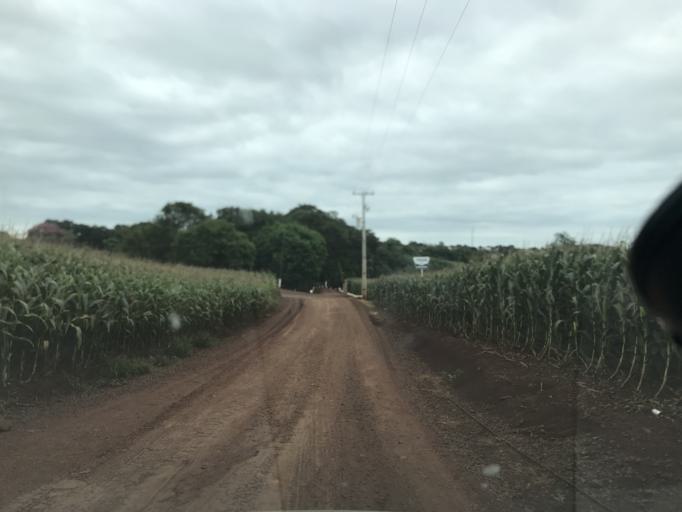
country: BR
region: Parana
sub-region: Palotina
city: Palotina
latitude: -24.3046
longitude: -53.8271
